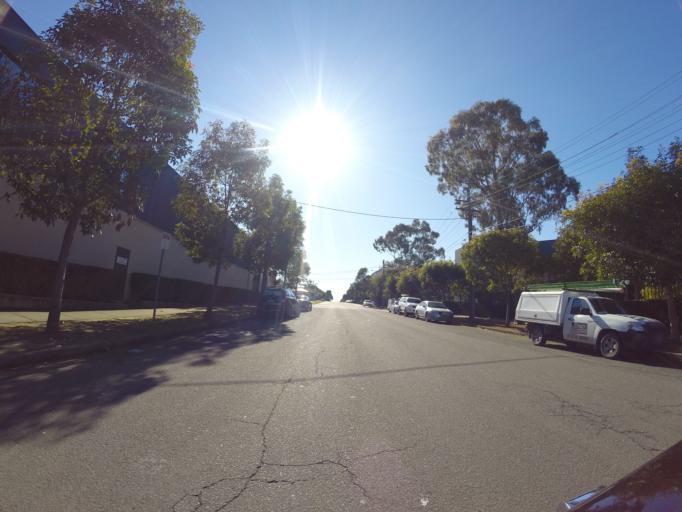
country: AU
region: New South Wales
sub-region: Auburn
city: Lidcombe
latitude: -33.8592
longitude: 151.0564
